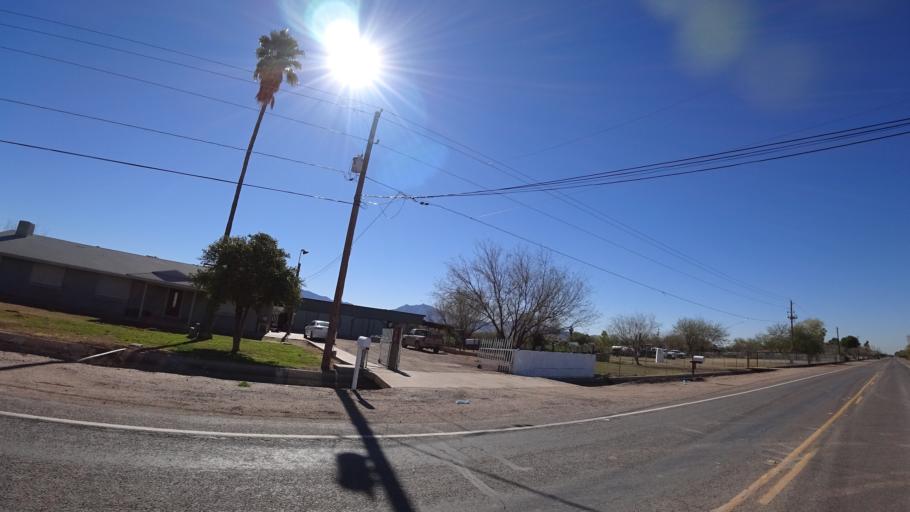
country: US
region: Arizona
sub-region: Maricopa County
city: Tolleson
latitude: 33.3922
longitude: -112.2748
